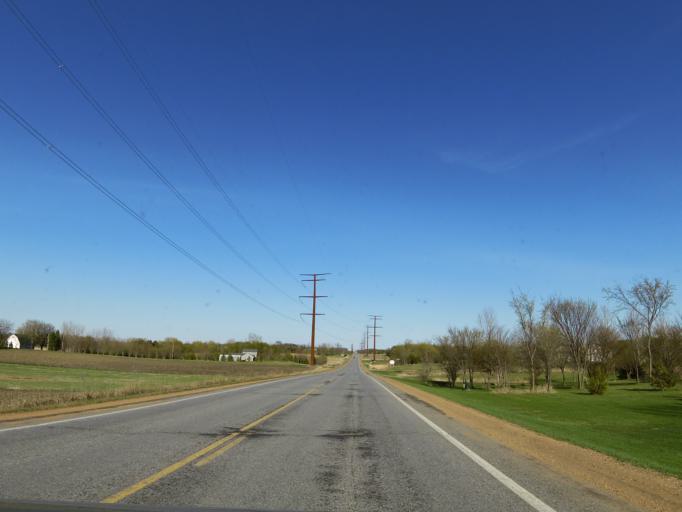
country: US
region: Minnesota
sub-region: Le Sueur County
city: New Prague
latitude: 44.5726
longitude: -93.4895
